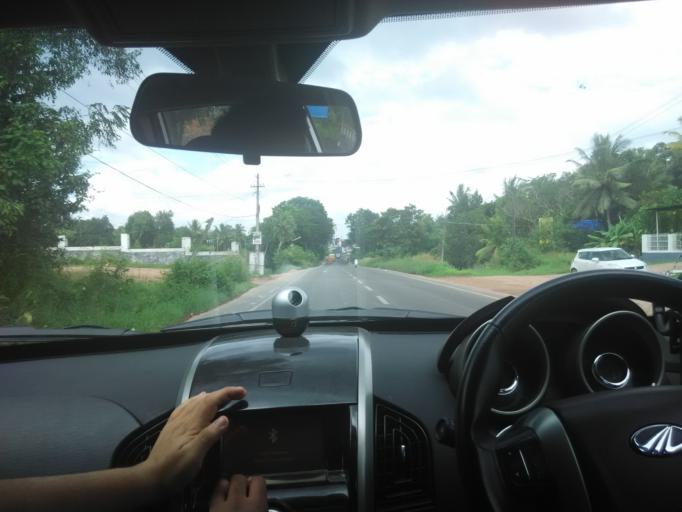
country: IN
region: Kerala
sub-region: Thiruvananthapuram
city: Attingal
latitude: 8.6393
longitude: 76.8449
